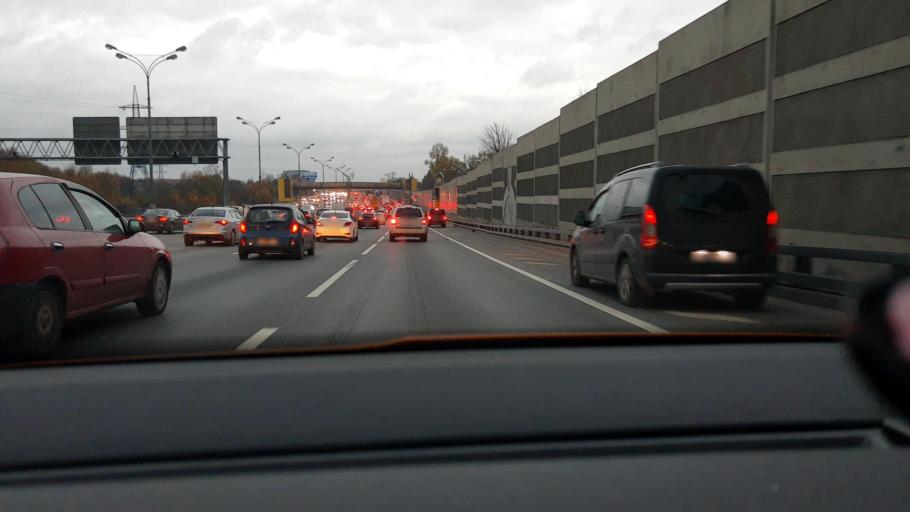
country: RU
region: Moscow
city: Yaroslavskiy
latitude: 55.8884
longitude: 37.7164
